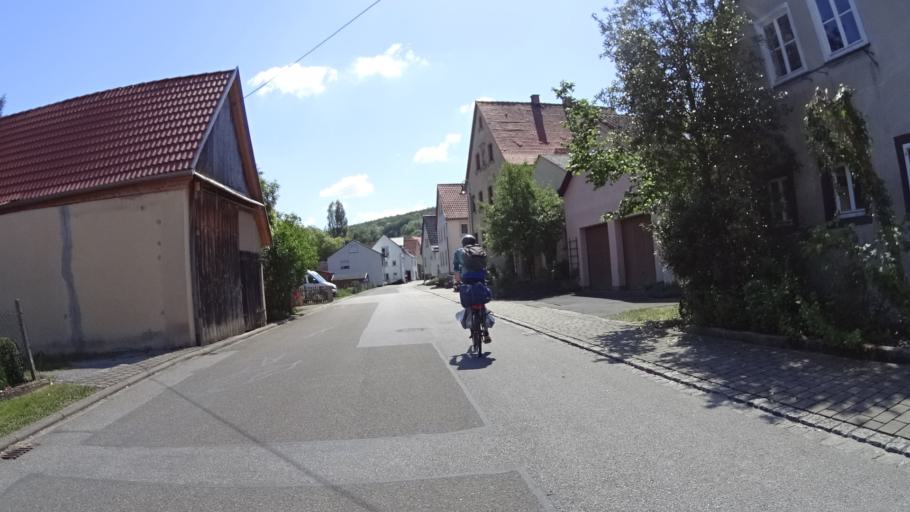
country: DE
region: Bavaria
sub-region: Regierungsbezirk Unterfranken
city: Tauberrettersheim
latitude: 49.4945
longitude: 9.9388
